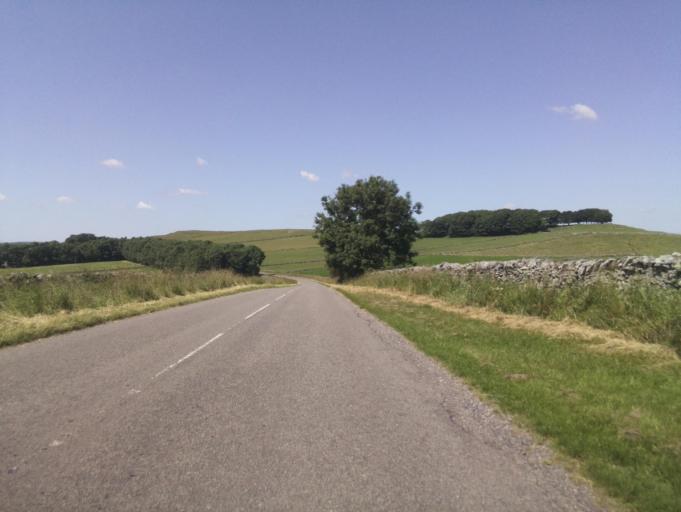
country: GB
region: England
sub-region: Derbyshire
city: Tideswell
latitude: 53.2749
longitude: -1.8318
